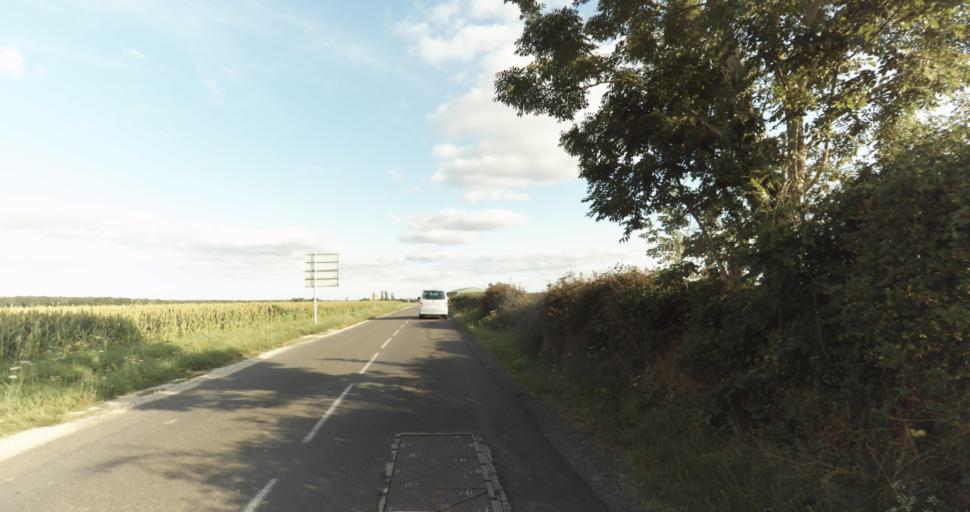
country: FR
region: Haute-Normandie
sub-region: Departement de l'Eure
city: Marcilly-sur-Eure
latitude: 48.9017
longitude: 1.2811
